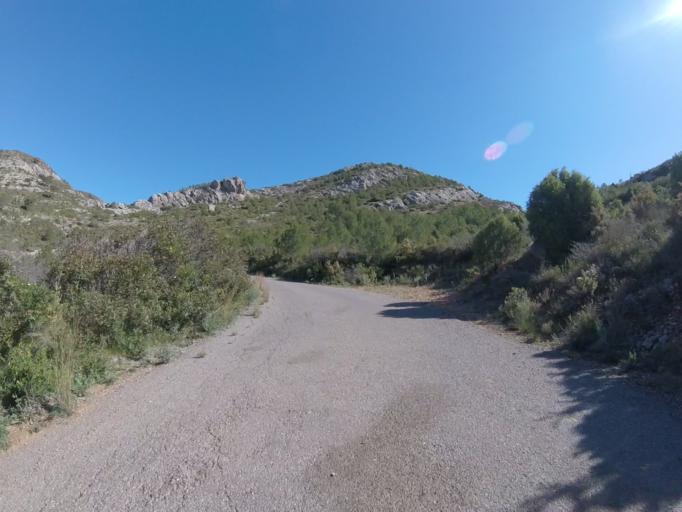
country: ES
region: Valencia
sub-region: Provincia de Castello
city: Benicassim
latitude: 40.0779
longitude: 0.1038
